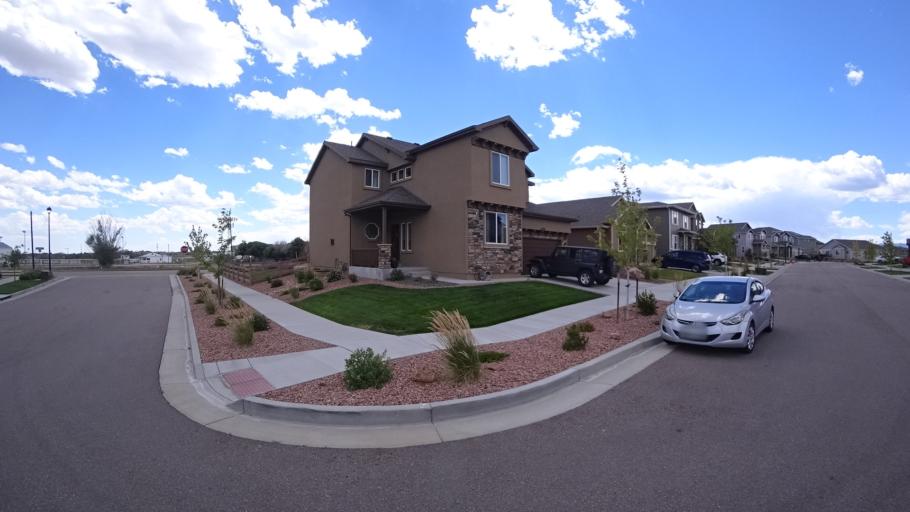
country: US
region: Colorado
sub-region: El Paso County
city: Black Forest
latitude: 38.9519
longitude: -104.7026
